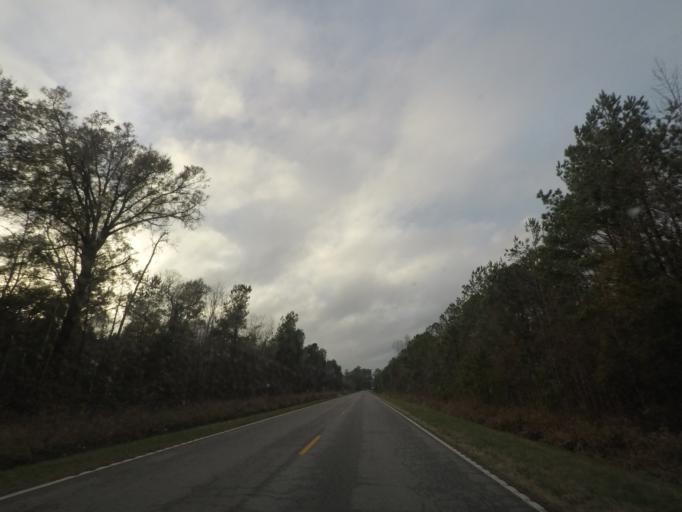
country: US
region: South Carolina
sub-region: Dorchester County
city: Saint George
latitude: 33.0495
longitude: -80.6056
